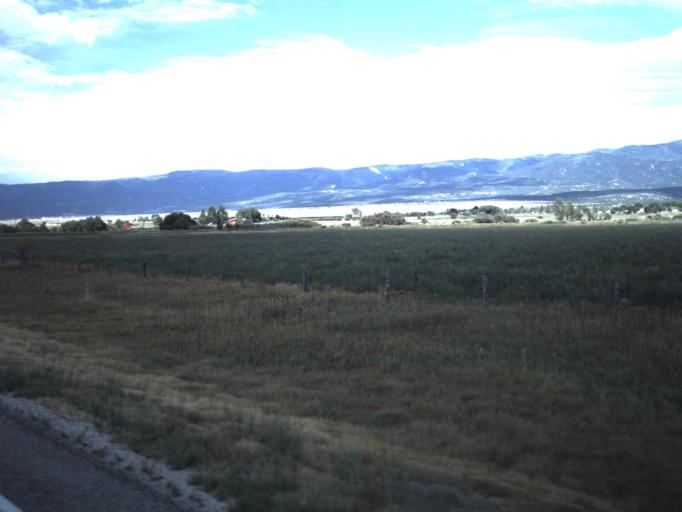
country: US
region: Utah
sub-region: Sanpete County
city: Moroni
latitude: 39.4849
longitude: -111.5186
